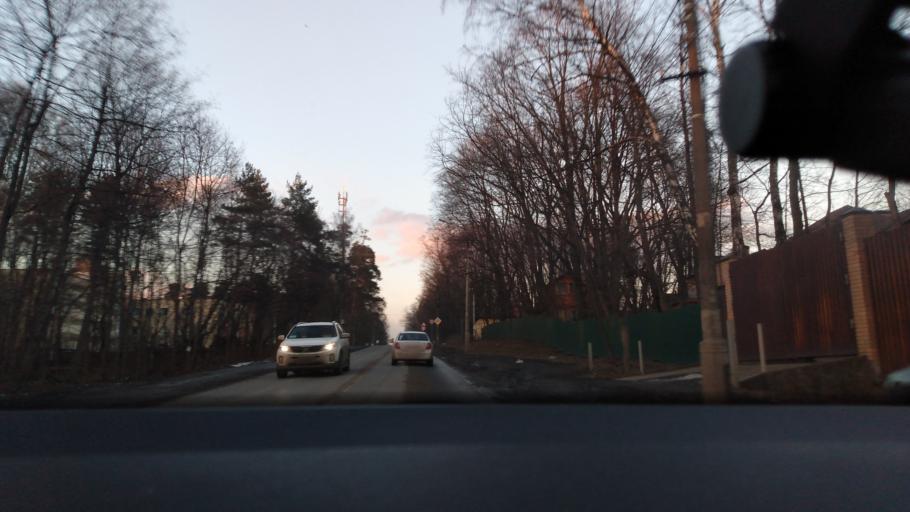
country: RU
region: Moskovskaya
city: Saltykovka
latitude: 55.7802
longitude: 37.9316
